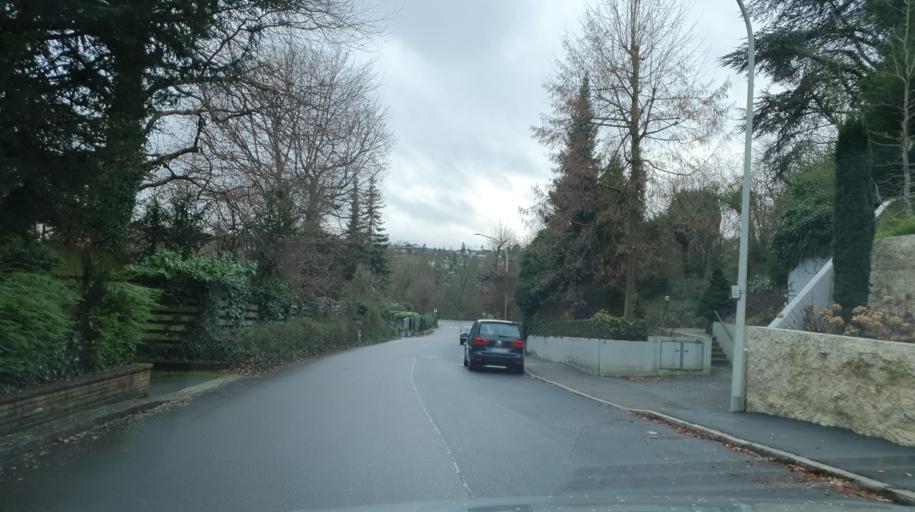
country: DE
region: Baden-Wuerttemberg
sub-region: Regierungsbezirk Stuttgart
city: Heilbronn
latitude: 49.1420
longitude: 9.2475
